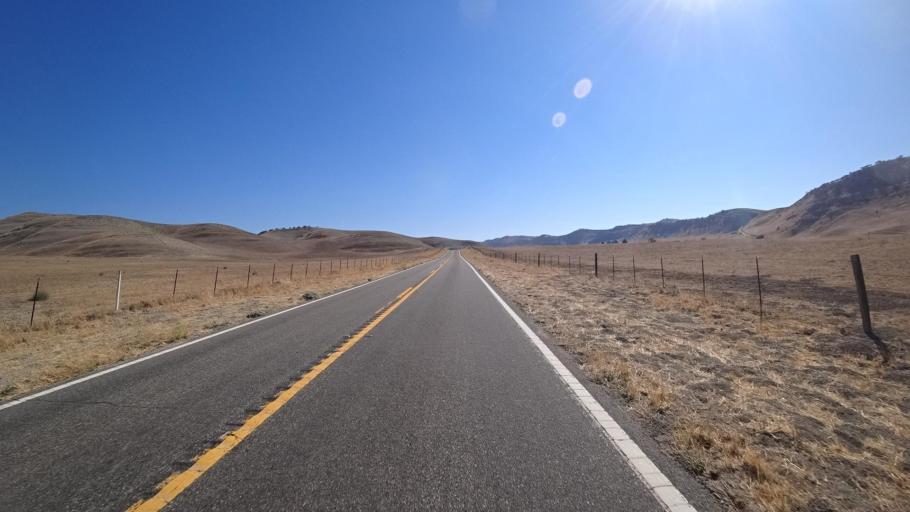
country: US
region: California
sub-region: Monterey County
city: King City
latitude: 36.1656
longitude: -120.8750
